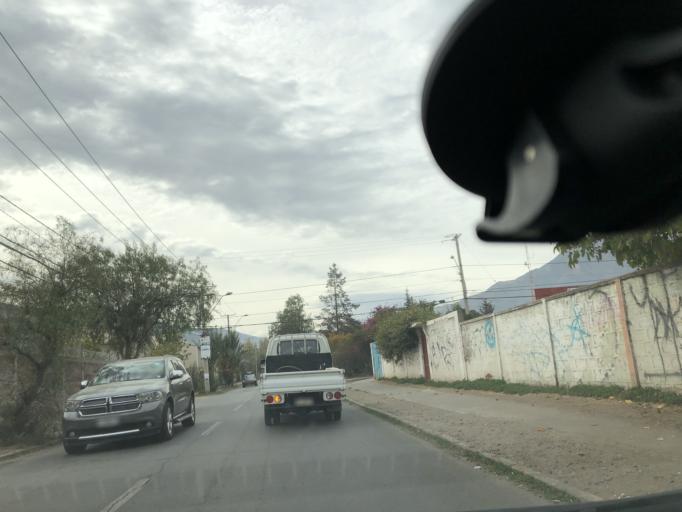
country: CL
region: Santiago Metropolitan
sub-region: Provincia de Cordillera
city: Puente Alto
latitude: -33.6080
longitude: -70.5226
